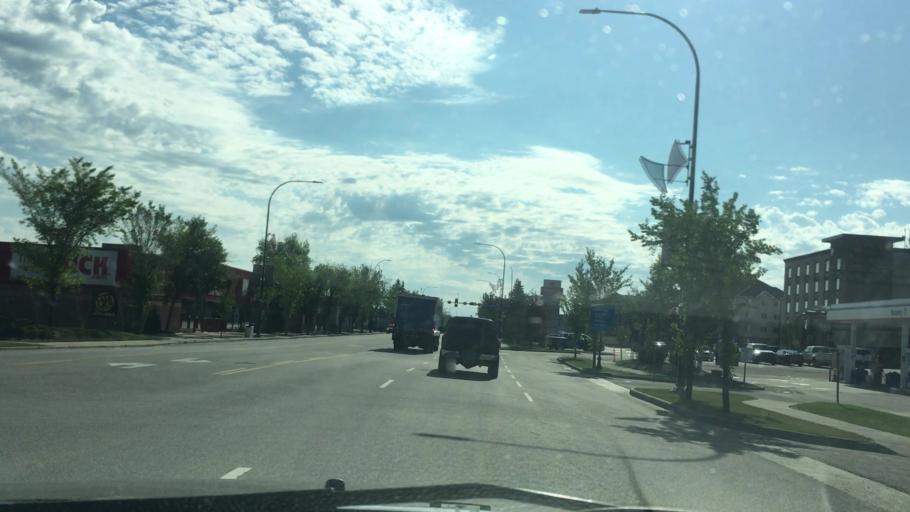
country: CA
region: Alberta
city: Leduc
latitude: 53.2647
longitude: -113.5603
